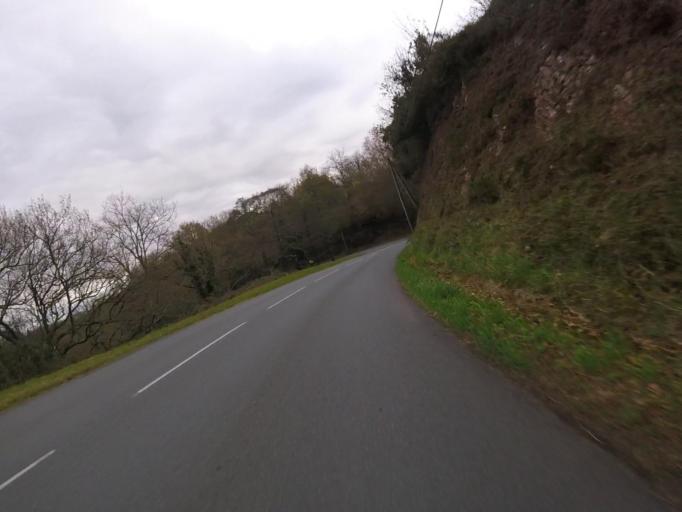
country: FR
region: Aquitaine
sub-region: Departement des Pyrenees-Atlantiques
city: Sare
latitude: 43.3159
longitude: -1.5942
